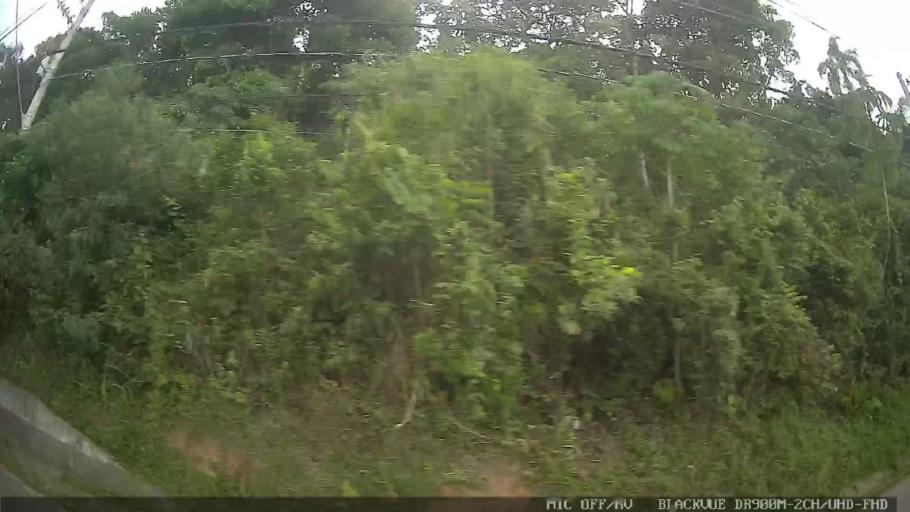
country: BR
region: Sao Paulo
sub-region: Suzano
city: Suzano
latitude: -23.6079
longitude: -46.2982
